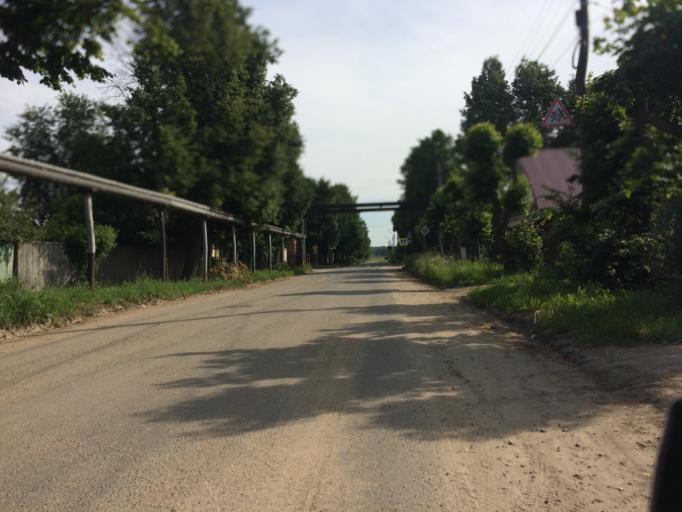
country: RU
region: Mariy-El
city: Yoshkar-Ola
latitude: 56.6502
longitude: 47.9127
